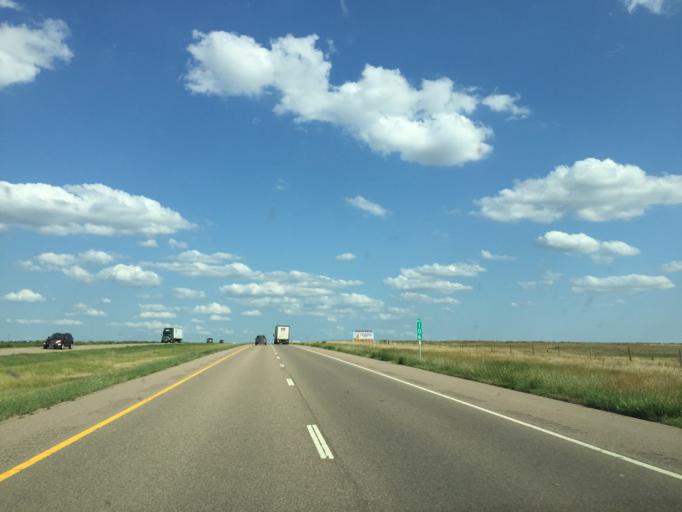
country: US
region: Kansas
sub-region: Gove County
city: Gove
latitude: 39.0695
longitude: -100.2665
